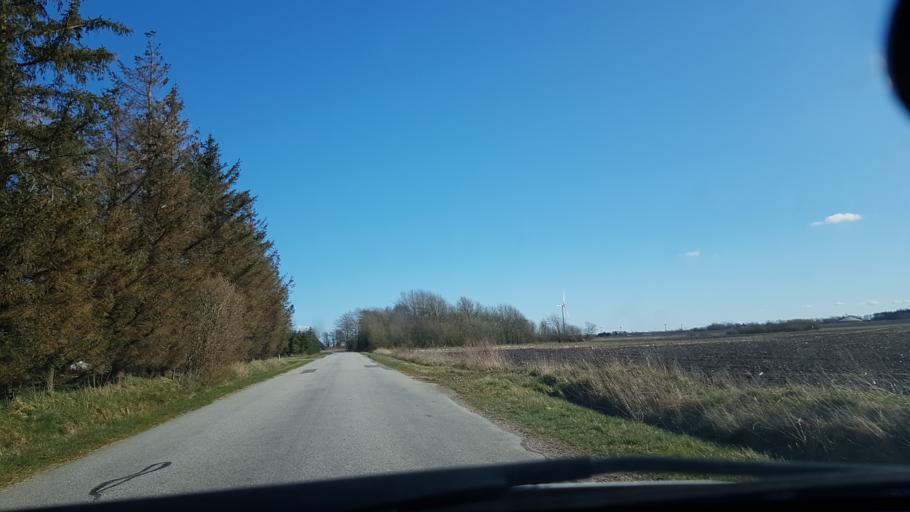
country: DK
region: South Denmark
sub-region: Tonder Kommune
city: Sherrebek
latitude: 55.2260
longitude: 8.8011
